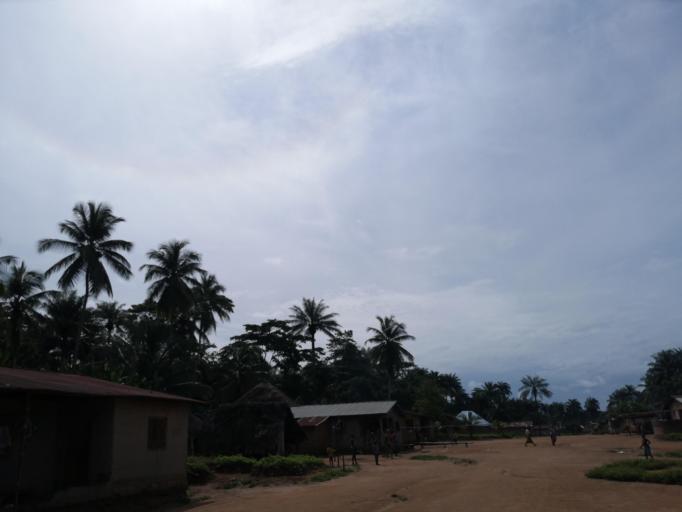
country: SL
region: Northern Province
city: Port Loko
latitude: 8.7914
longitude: -12.9348
